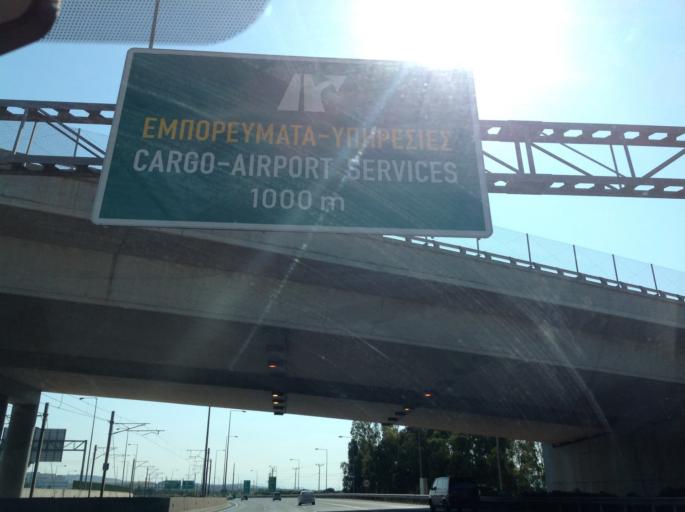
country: GR
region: Attica
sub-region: Nomarchia Anatolikis Attikis
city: Markopoulo
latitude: 37.9143
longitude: 23.9200
